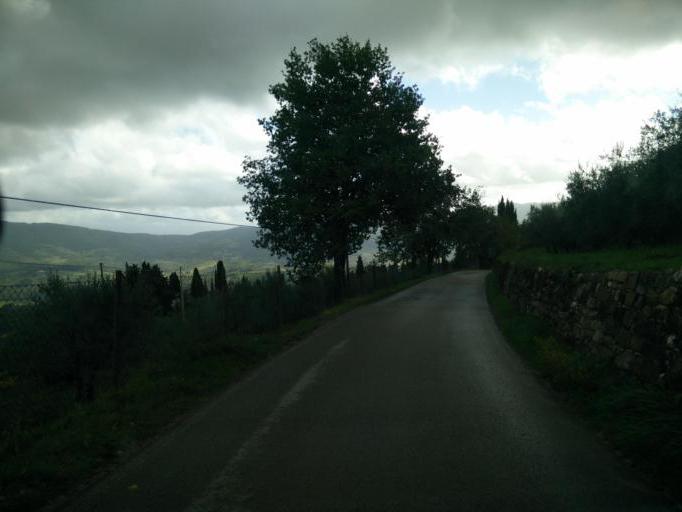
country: IT
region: Tuscany
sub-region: Province of Florence
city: Greve in Chianti
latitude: 43.5811
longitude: 11.2821
